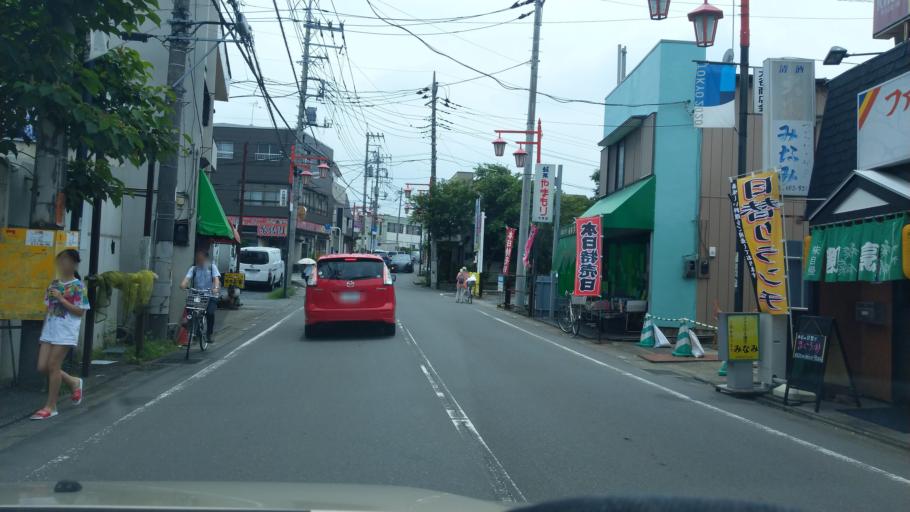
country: JP
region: Saitama
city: Saitama
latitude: 35.9273
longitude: 139.6687
